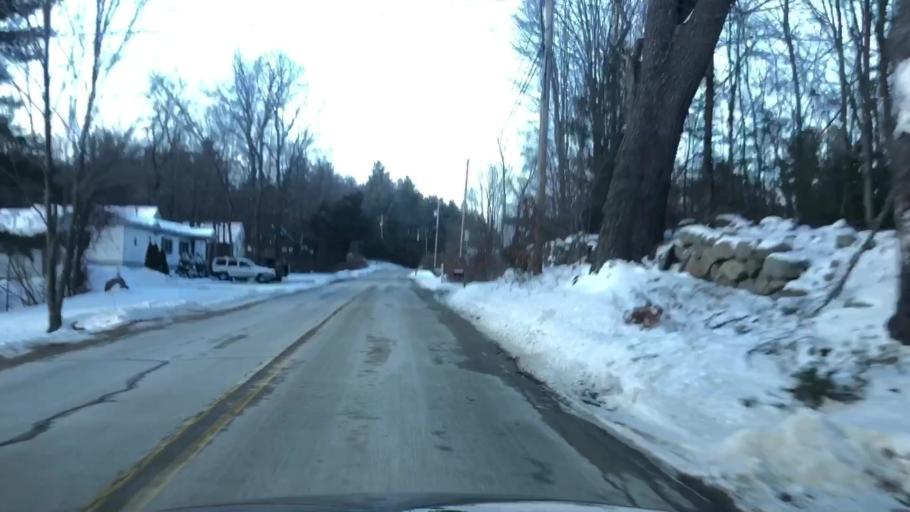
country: US
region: New Hampshire
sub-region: Hillsborough County
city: Milford
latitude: 42.8112
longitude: -71.6683
